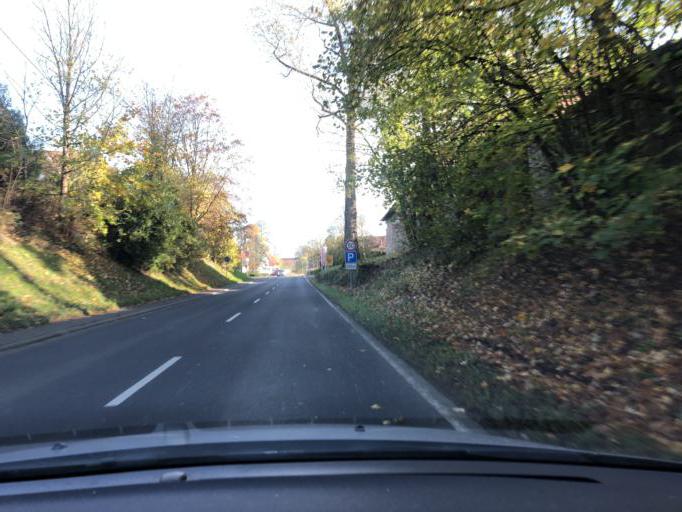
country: DE
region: Thuringia
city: Kloster Vessra
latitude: 50.4919
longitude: 10.6423
